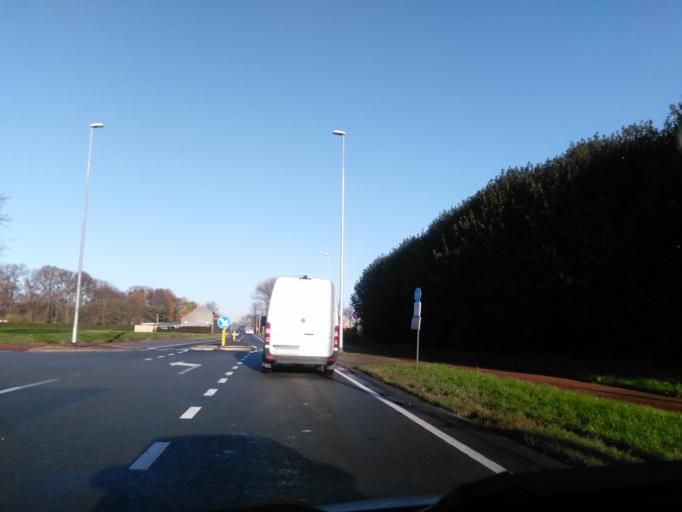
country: BE
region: Flanders
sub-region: Provincie Antwerpen
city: Zwijndrecht
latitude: 51.2071
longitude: 4.3158
